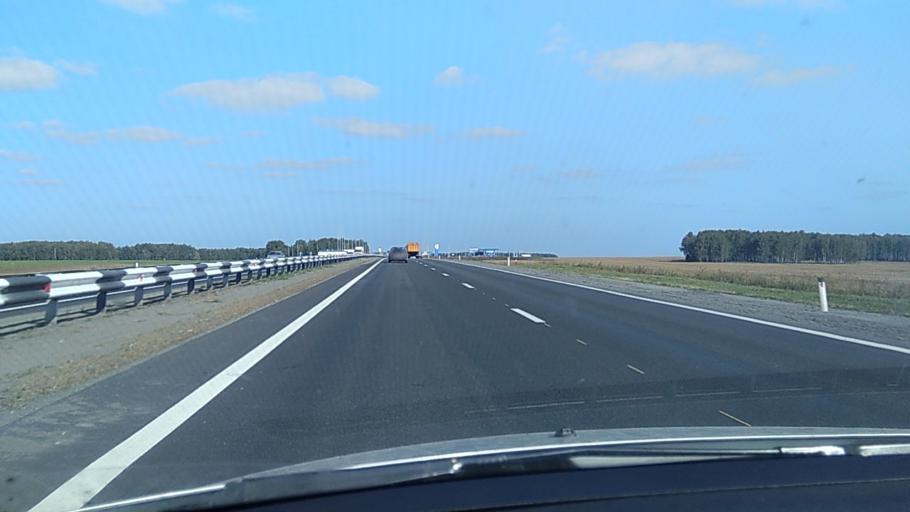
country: RU
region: Chelyabinsk
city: Timiryazevskiy
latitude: 54.9500
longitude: 60.8592
